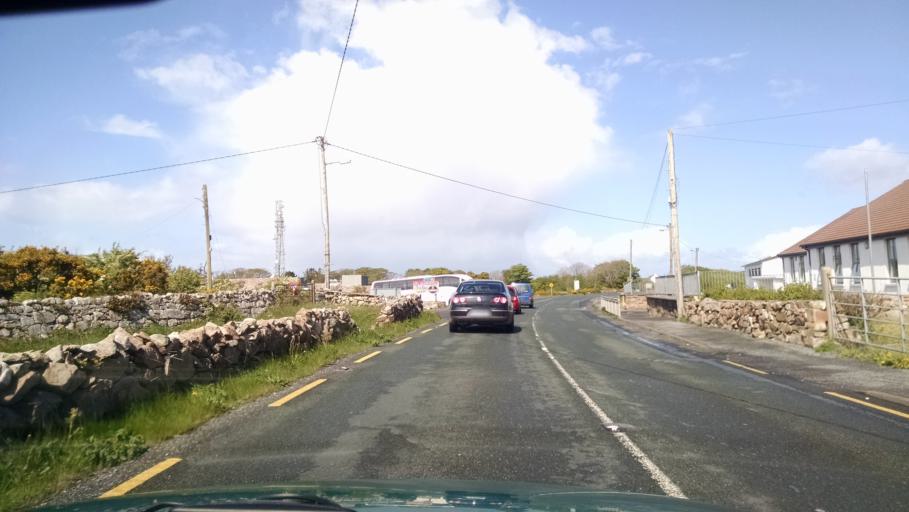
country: IE
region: Connaught
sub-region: County Galway
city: Oughterard
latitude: 53.2369
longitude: -9.4920
